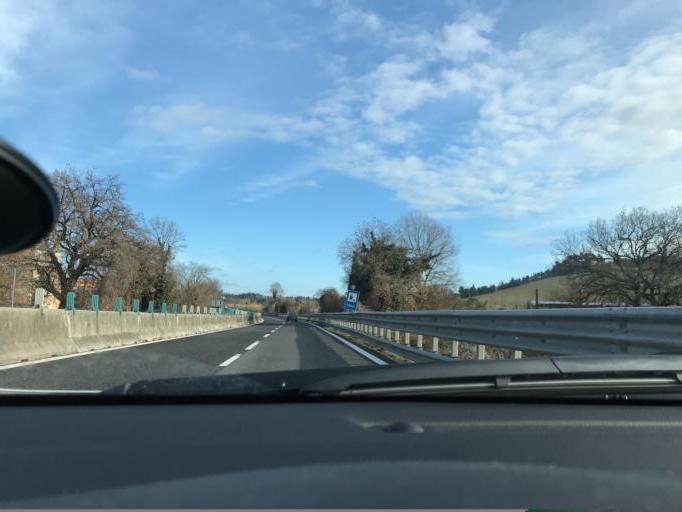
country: IT
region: The Marches
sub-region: Provincia di Ancona
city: Falconara Marittima
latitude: 43.6001
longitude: 13.3614
